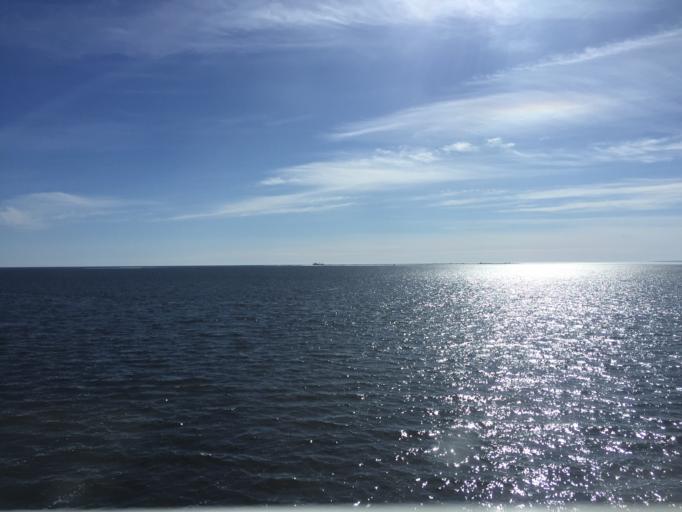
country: EE
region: Saare
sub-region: Orissaare vald
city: Orissaare
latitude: 58.5753
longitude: 23.4384
